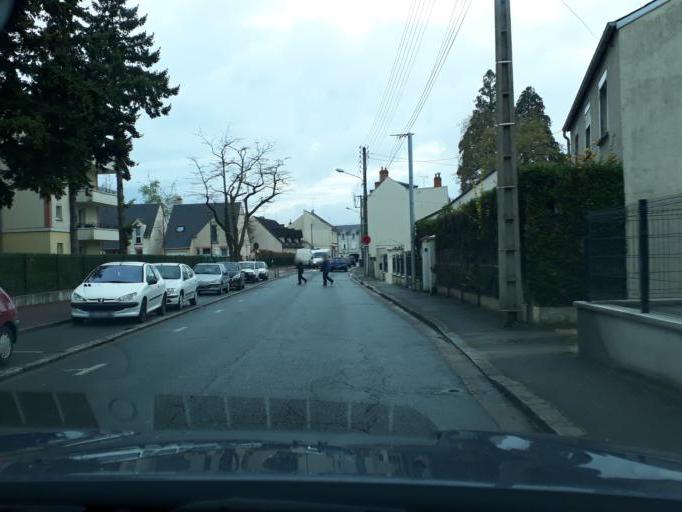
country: FR
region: Centre
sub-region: Departement du Loiret
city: Saint-Jean-de-la-Ruelle
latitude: 47.9118
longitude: 1.8815
